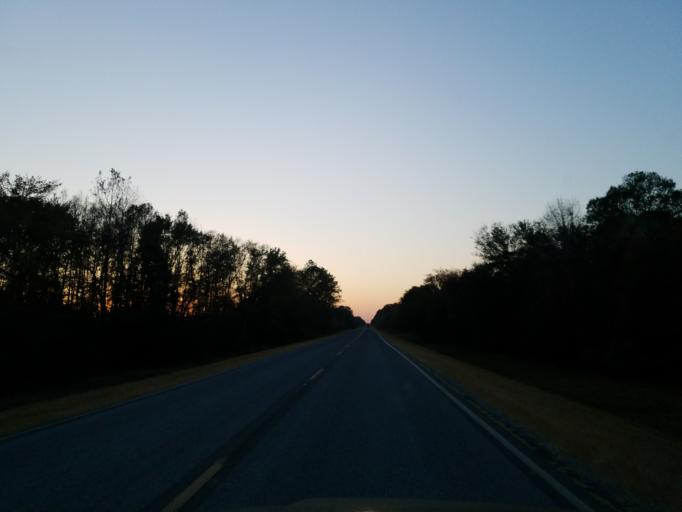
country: US
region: Georgia
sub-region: Ben Hill County
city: Fitzgerald
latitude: 31.7210
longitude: -83.4484
